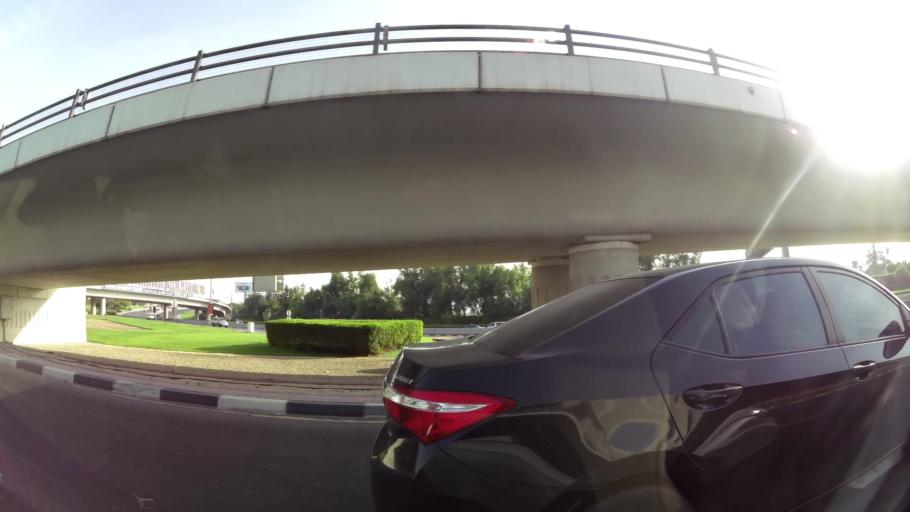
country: AE
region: Ash Shariqah
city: Sharjah
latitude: 25.2405
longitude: 55.3407
